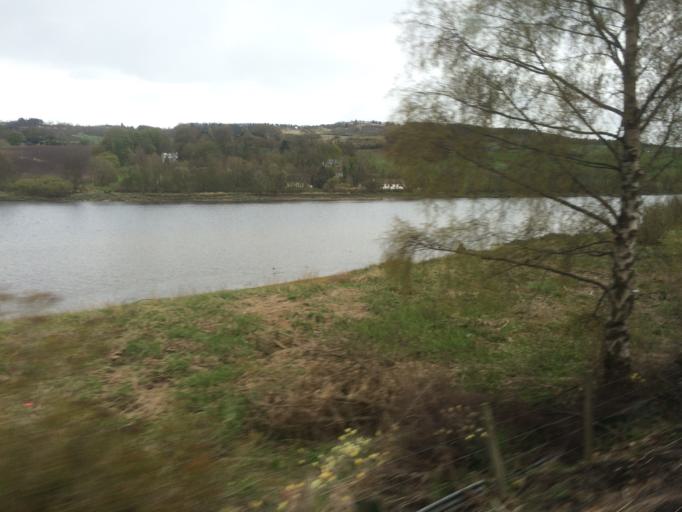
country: GB
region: Scotland
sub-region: Perth and Kinross
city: Bridge of Earn
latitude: 56.3832
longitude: -3.3947
